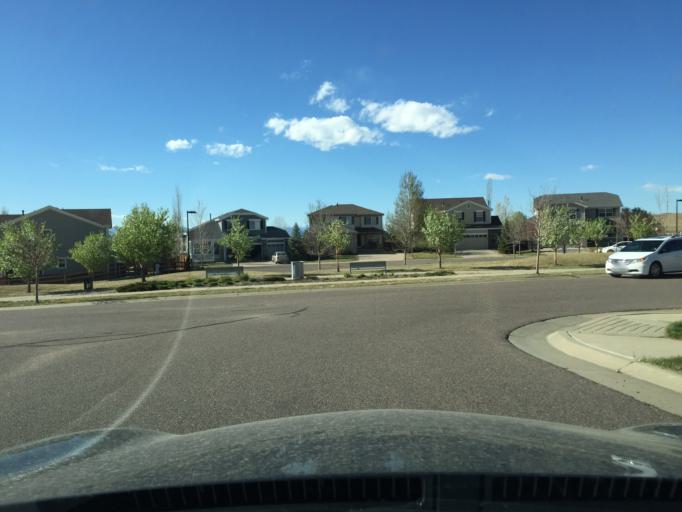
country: US
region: Colorado
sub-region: Boulder County
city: Erie
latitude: 40.0089
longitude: -105.0296
